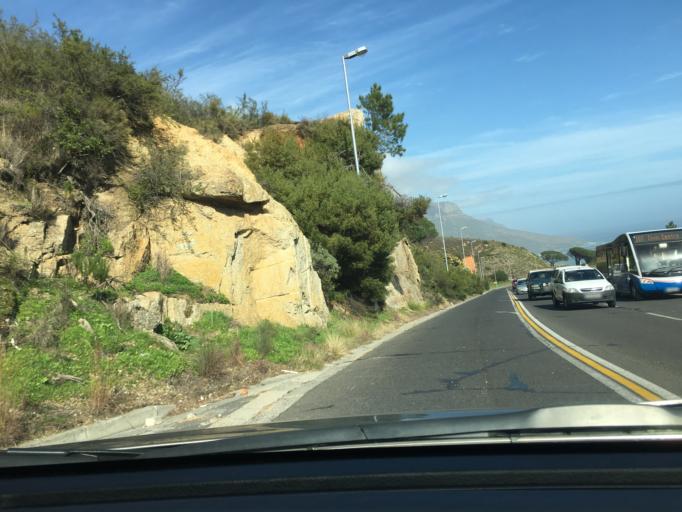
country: ZA
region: Western Cape
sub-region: City of Cape Town
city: Cape Town
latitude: -33.9465
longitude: 18.3923
